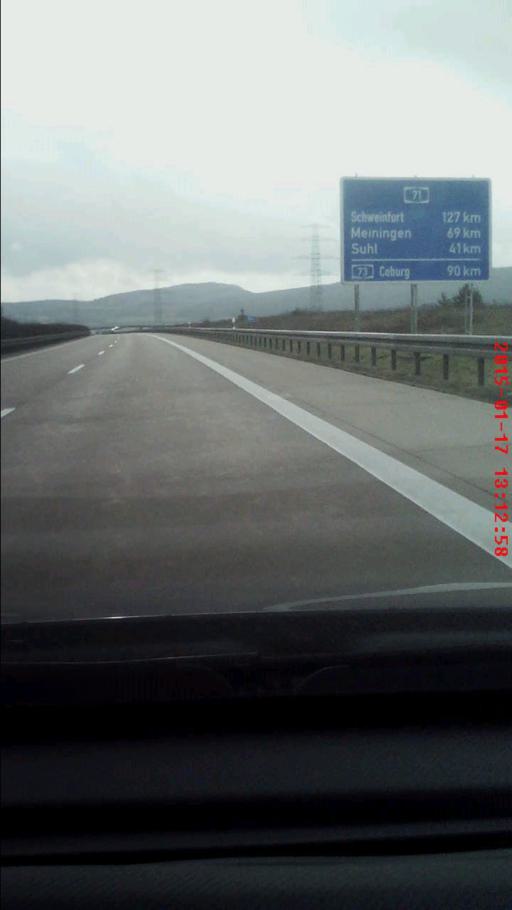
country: DE
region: Thuringia
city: Dornheim
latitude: 50.8163
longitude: 11.0013
